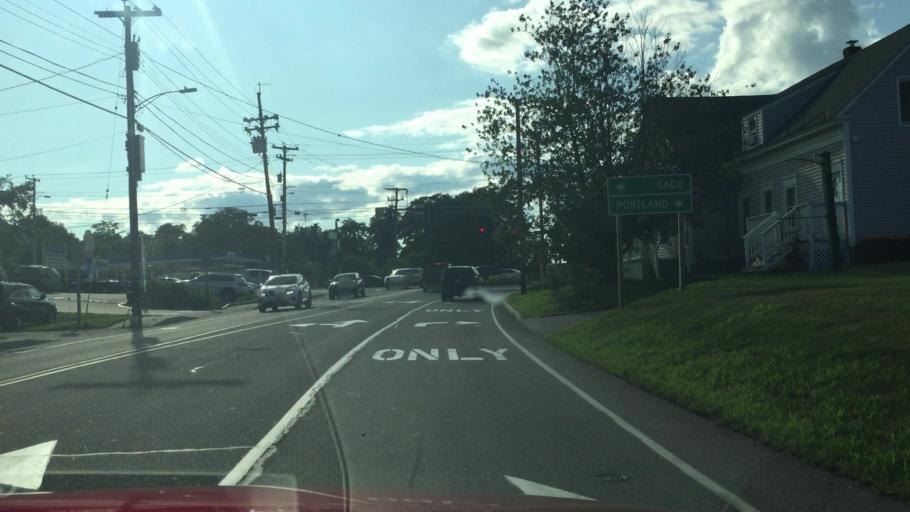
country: US
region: Maine
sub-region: Cumberland County
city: West Scarborough
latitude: 43.5705
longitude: -70.3867
